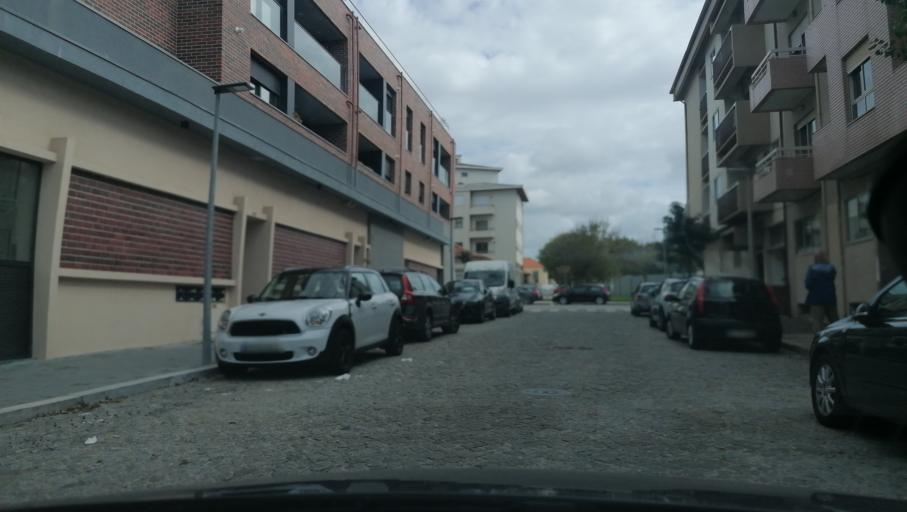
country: PT
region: Aveiro
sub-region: Espinho
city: Espinho
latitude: 41.0012
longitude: -8.6406
